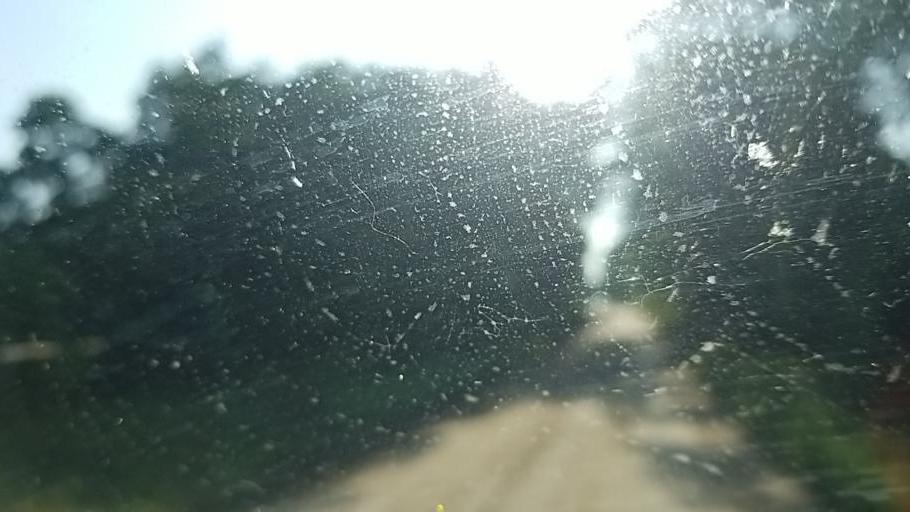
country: US
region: Michigan
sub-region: Newaygo County
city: Newaygo
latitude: 43.3799
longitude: -85.8343
